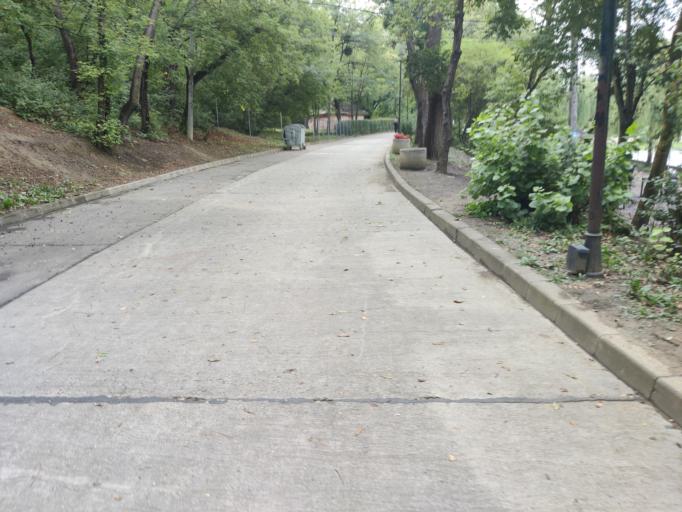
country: RO
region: Iasi
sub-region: Municipiul Iasi
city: Iasi
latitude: 47.1816
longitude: 27.6032
